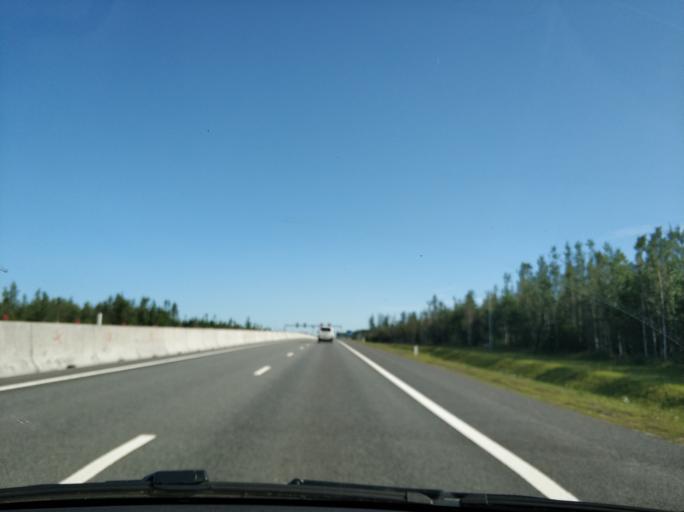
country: RU
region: Leningrad
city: Sosnovo
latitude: 60.4682
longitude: 30.1961
